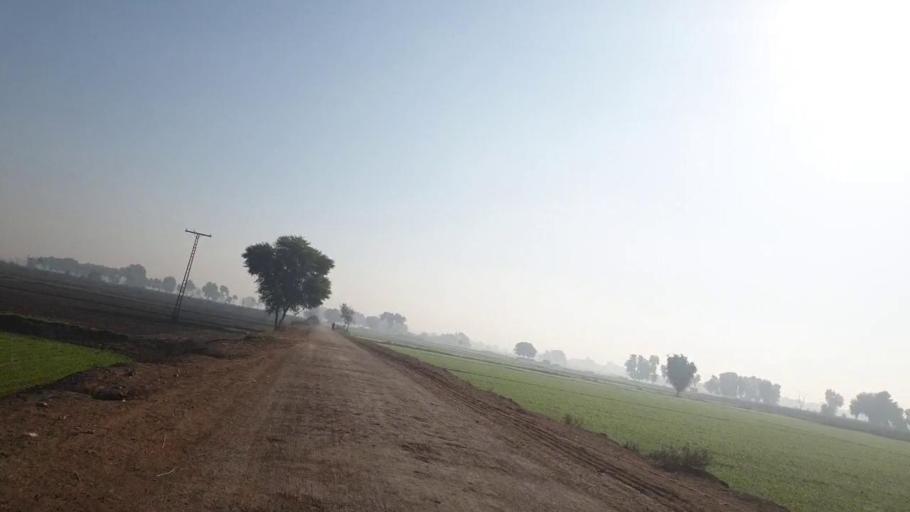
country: PK
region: Sindh
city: Dadu
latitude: 26.6757
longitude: 67.7864
